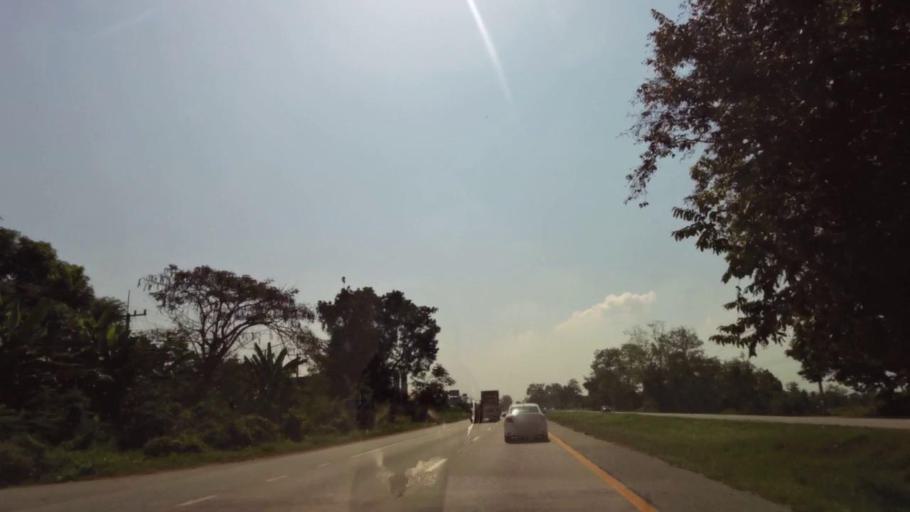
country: TH
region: Phichit
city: Wachira Barami
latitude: 16.6008
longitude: 100.1478
